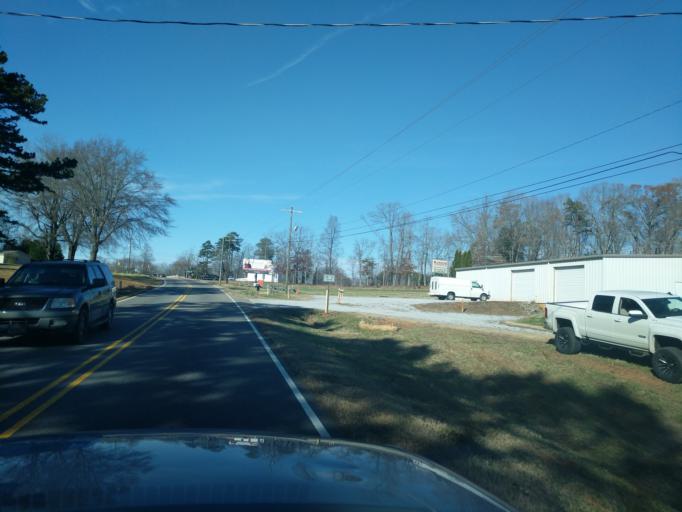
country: US
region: North Carolina
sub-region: Rutherford County
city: Spindale
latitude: 35.3215
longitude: -81.9332
